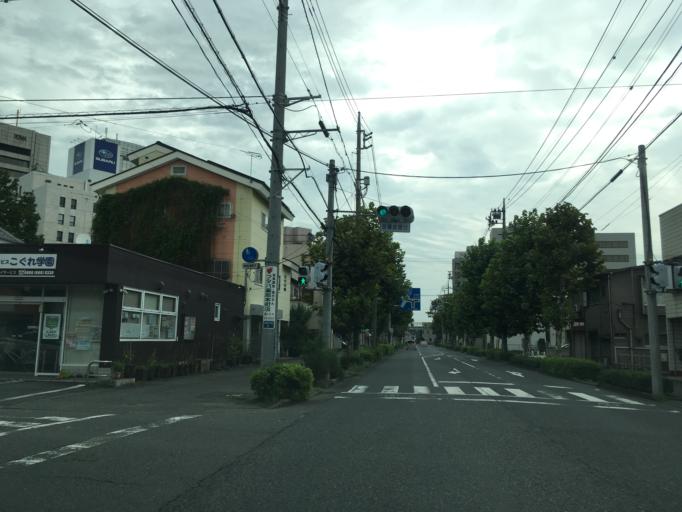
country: JP
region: Gunma
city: Maebashi-shi
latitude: 36.3882
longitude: 139.0701
